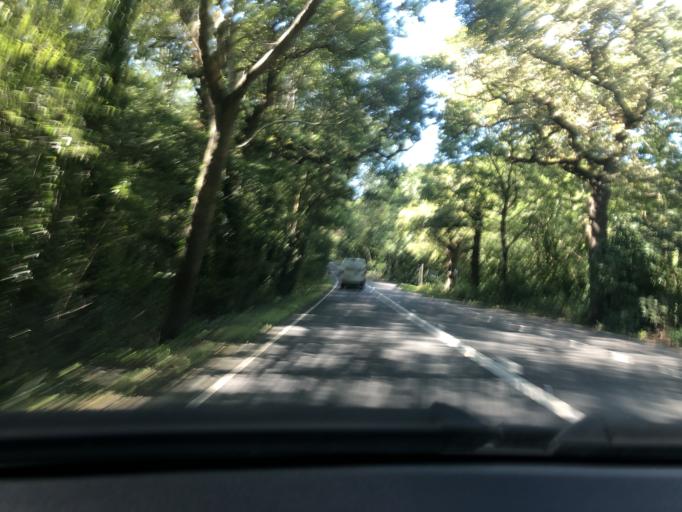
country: GB
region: England
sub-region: Somerset
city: Westonzoyland
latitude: 51.1339
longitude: -2.8525
